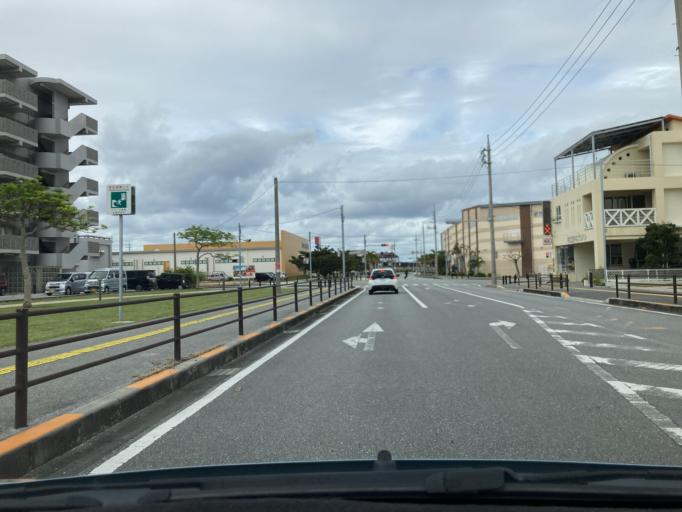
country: JP
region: Okinawa
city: Itoman
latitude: 26.1571
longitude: 127.6600
